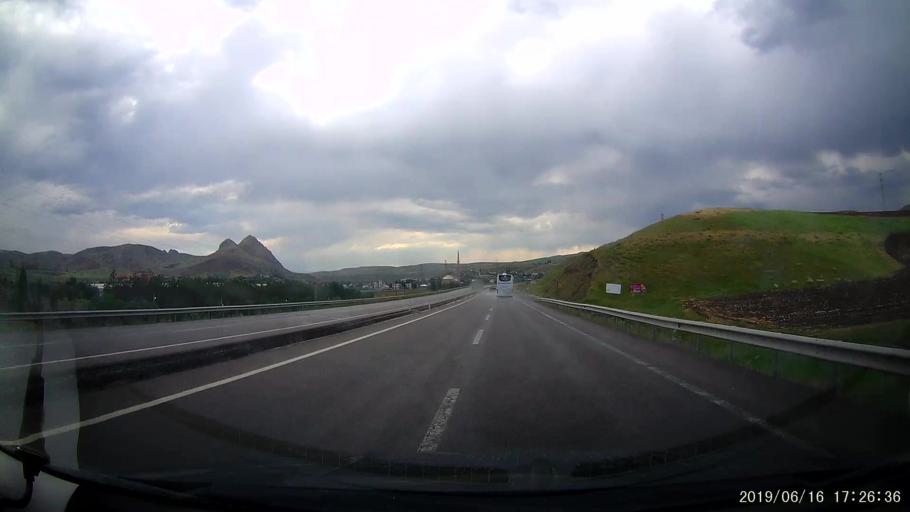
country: TR
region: Erzincan
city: Tercan
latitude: 39.7692
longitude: 40.4089
